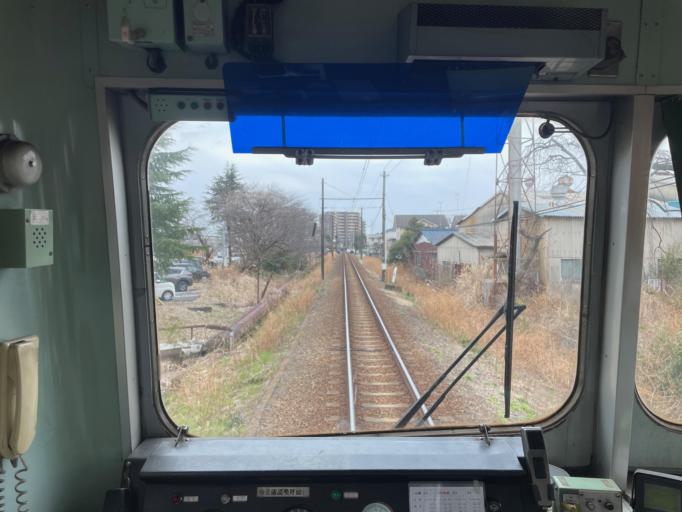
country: JP
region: Shizuoka
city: Fuji
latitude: 35.1648
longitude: 138.7016
